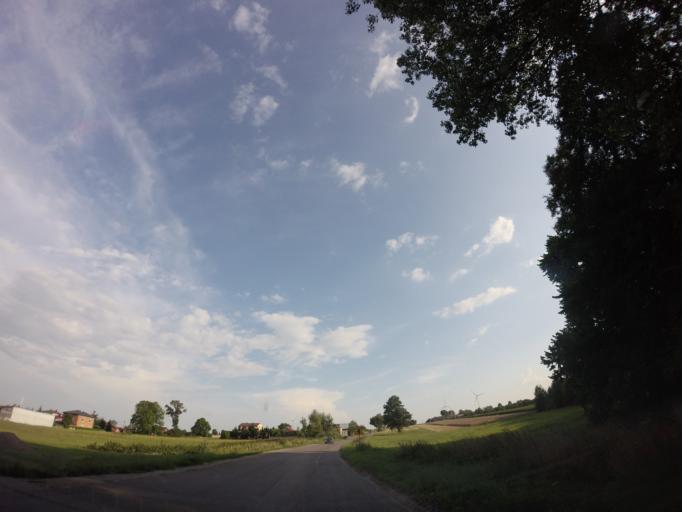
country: PL
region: Lublin Voivodeship
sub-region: Powiat lubartowski
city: Michow
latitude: 51.5188
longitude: 22.3112
